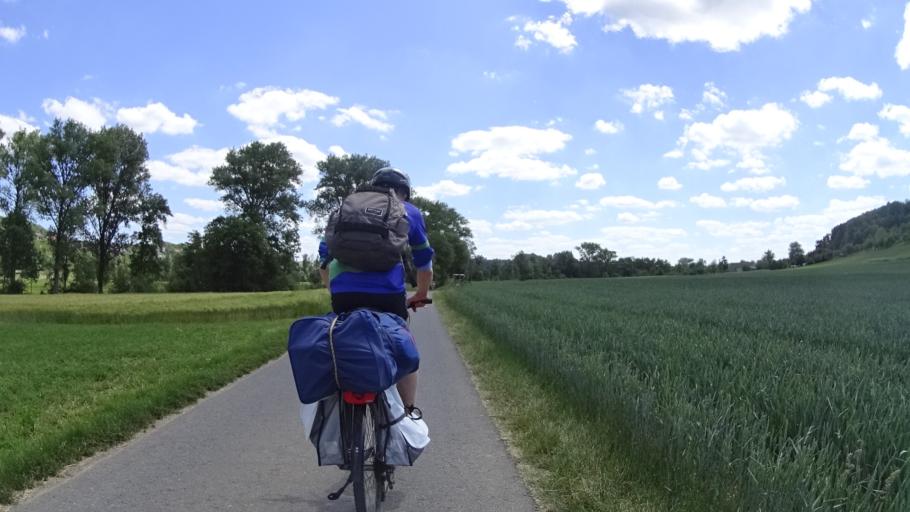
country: DE
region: Bavaria
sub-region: Regierungsbezirk Unterfranken
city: Bieberehren
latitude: 49.5189
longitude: 9.9993
